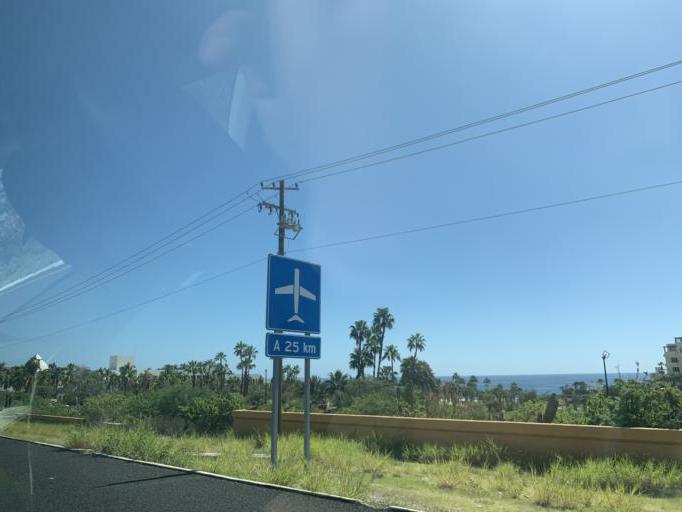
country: MX
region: Baja California Sur
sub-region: Los Cabos
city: San Jose del Cabo
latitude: 22.9802
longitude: -109.7700
